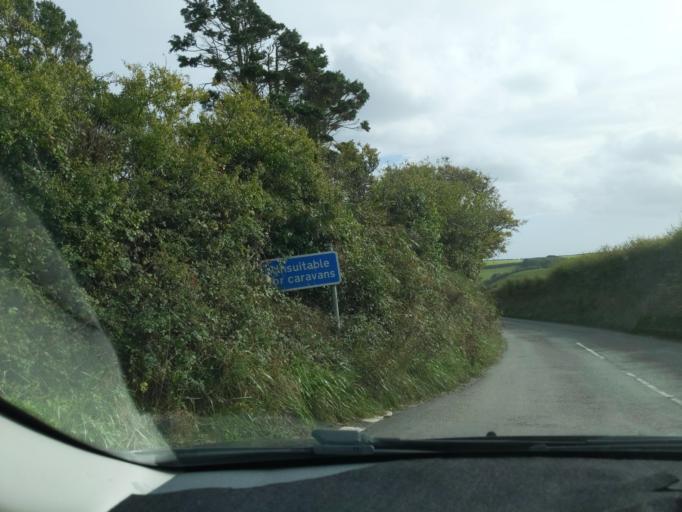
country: GB
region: England
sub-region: Cornwall
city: Mevagissey
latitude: 50.2452
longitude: -4.8012
